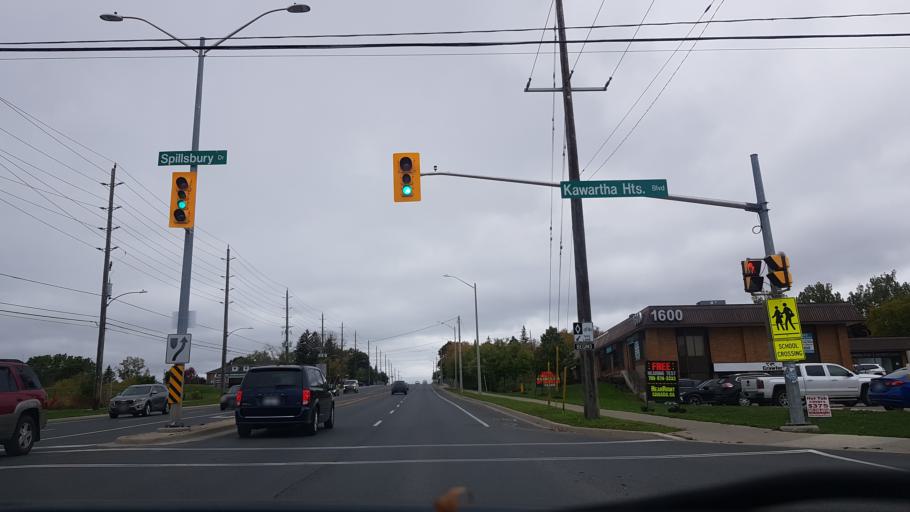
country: CA
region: Ontario
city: Peterborough
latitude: 44.2773
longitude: -78.3650
